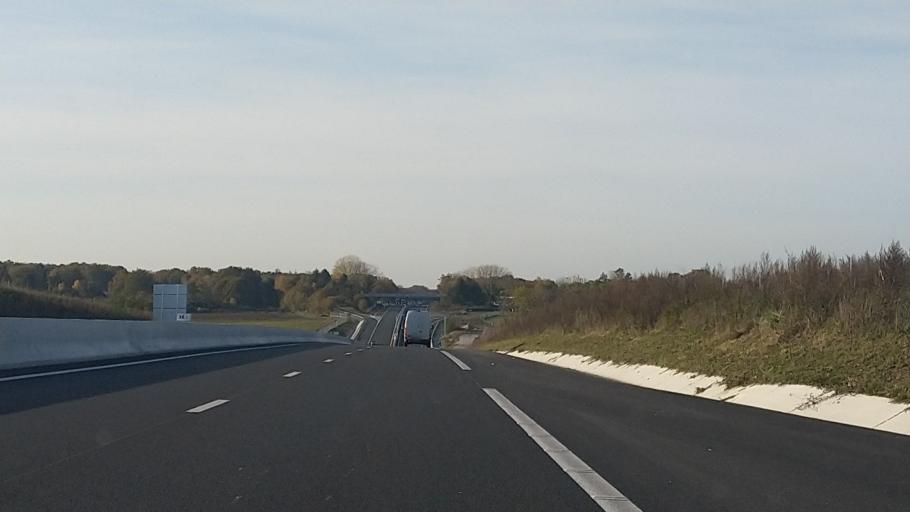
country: FR
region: Ile-de-France
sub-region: Departement du Val-d'Oise
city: Maffliers
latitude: 49.0987
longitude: 2.2884
